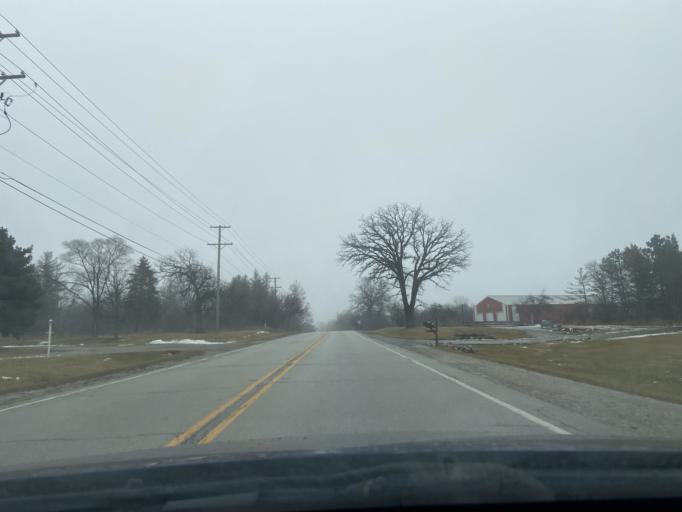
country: US
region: Illinois
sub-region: Lake County
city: Volo
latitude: 42.3197
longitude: -88.1362
